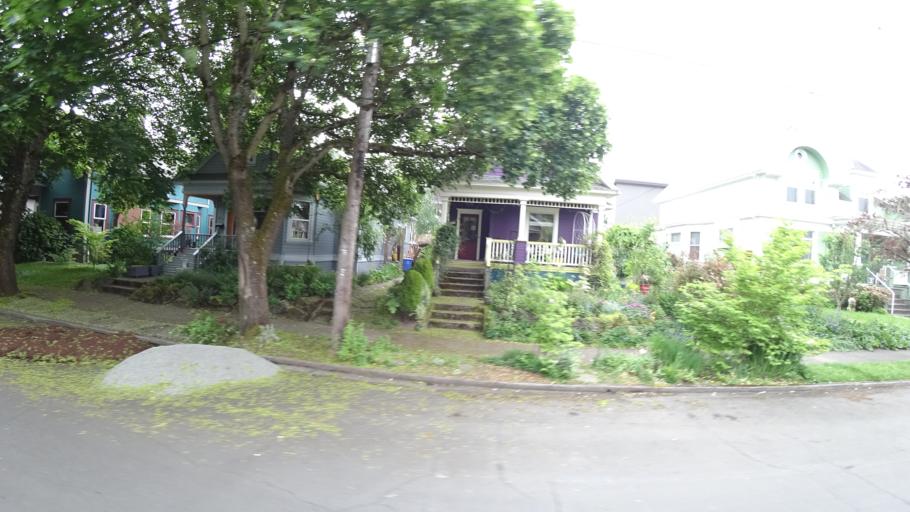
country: US
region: Oregon
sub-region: Multnomah County
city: Portland
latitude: 45.5172
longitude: -122.6254
